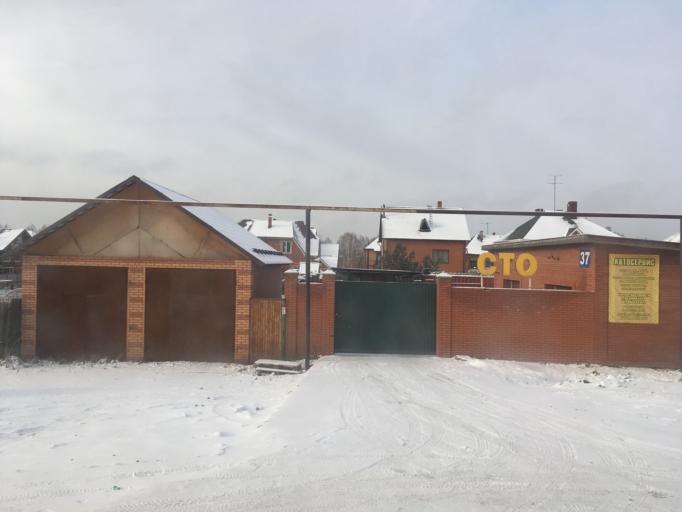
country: RU
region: Novosibirsk
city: Mochishche
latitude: 55.0828
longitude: 83.0402
